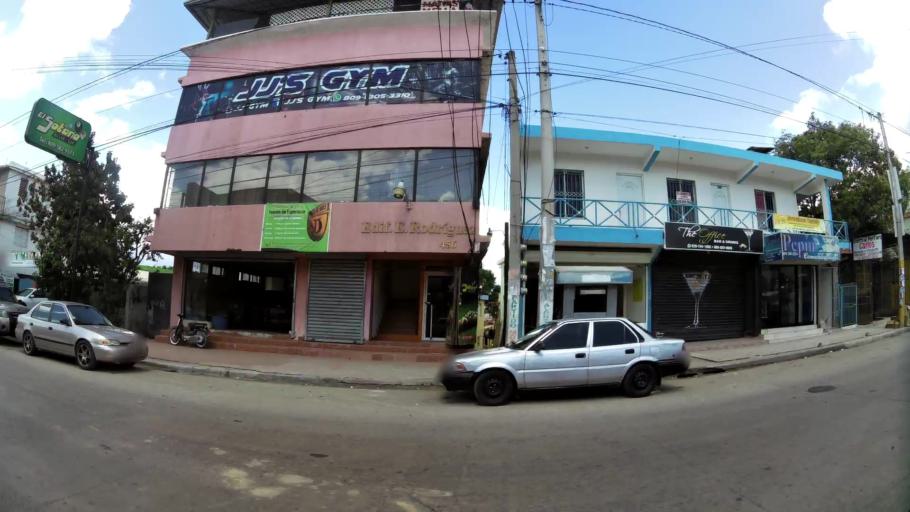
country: DO
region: Santiago
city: Santiago de los Caballeros
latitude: 19.4271
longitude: -70.6861
